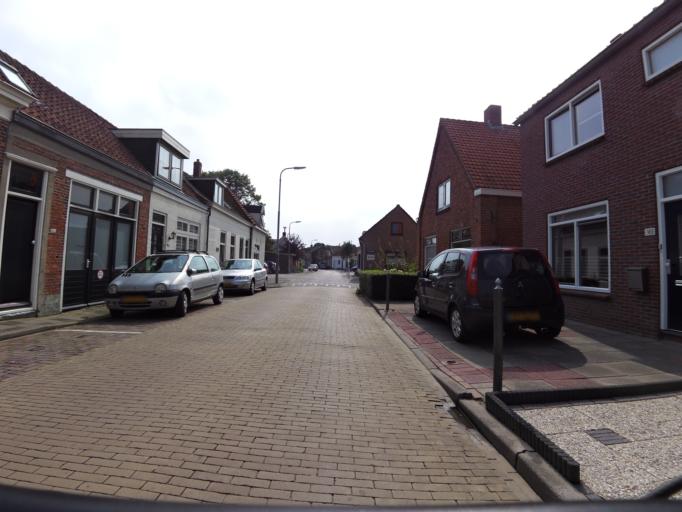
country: NL
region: Zeeland
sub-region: Gemeente Middelburg
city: Middelburg
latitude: 51.5166
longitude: 3.6052
